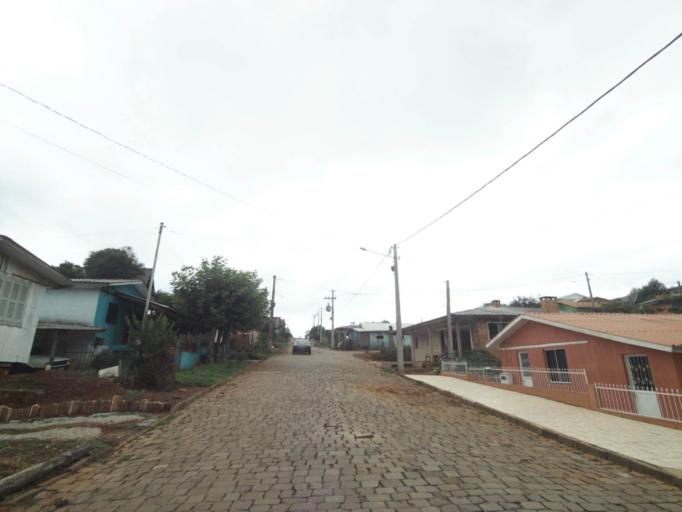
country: BR
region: Rio Grande do Sul
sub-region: Lagoa Vermelha
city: Lagoa Vermelha
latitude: -28.2133
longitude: -51.5045
